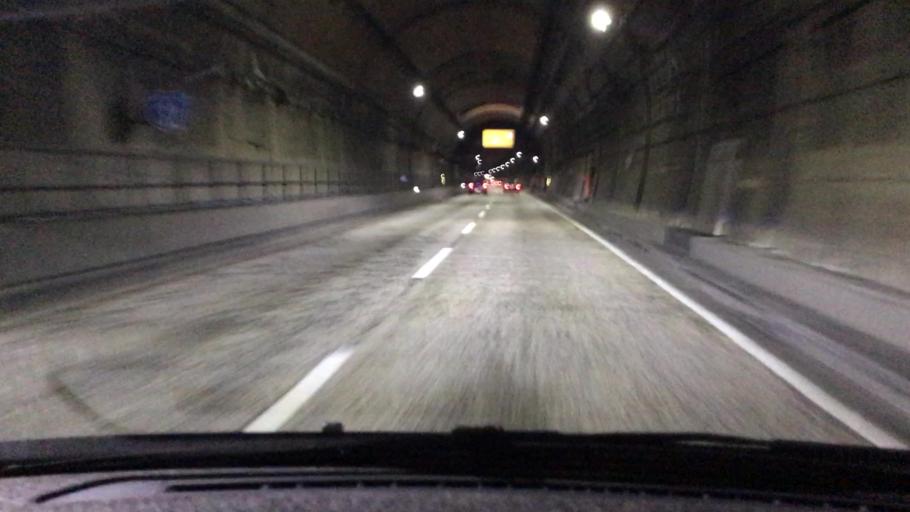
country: JP
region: Hyogo
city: Kobe
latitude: 34.7155
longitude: 135.1890
